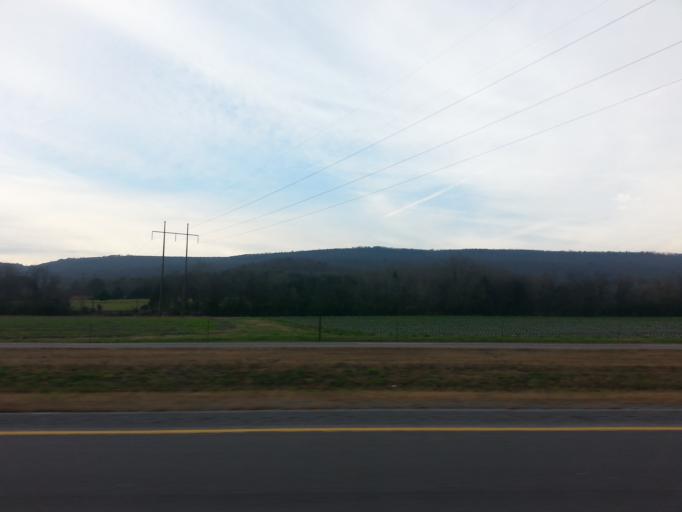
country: US
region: Tennessee
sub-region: Rhea County
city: Spring City
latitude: 35.6240
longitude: -84.9035
